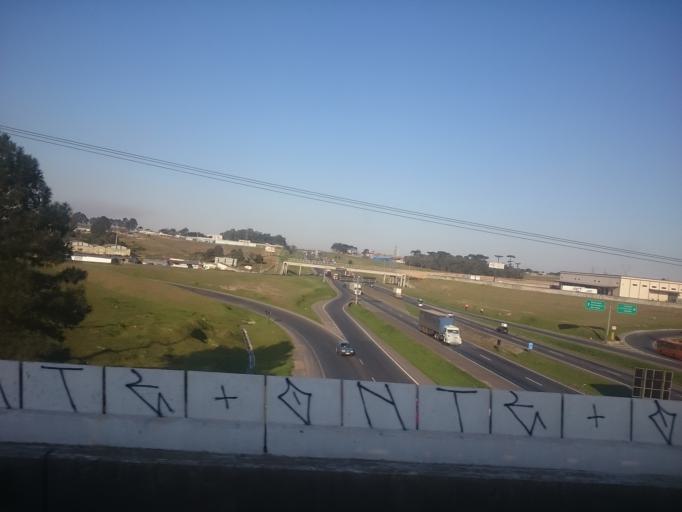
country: BR
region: Parana
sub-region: Sao Jose Dos Pinhais
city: Sao Jose dos Pinhais
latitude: -25.5441
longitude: -49.3031
